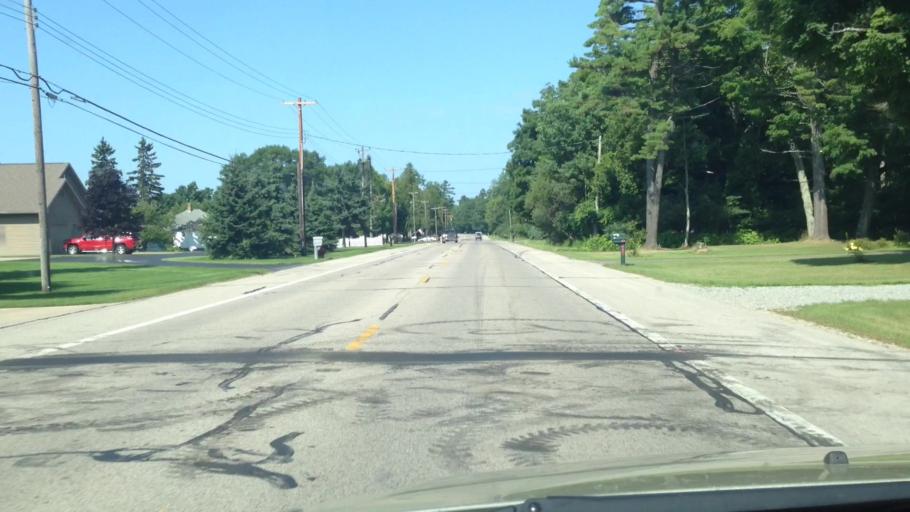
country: US
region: Michigan
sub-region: Delta County
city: Escanaba
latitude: 45.6867
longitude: -87.1091
